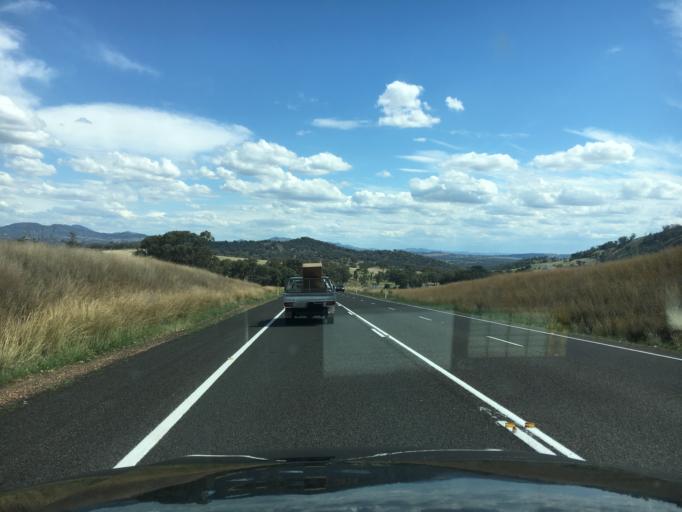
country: AU
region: New South Wales
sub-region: Liverpool Plains
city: Quirindi
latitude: -31.5039
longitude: 150.8622
